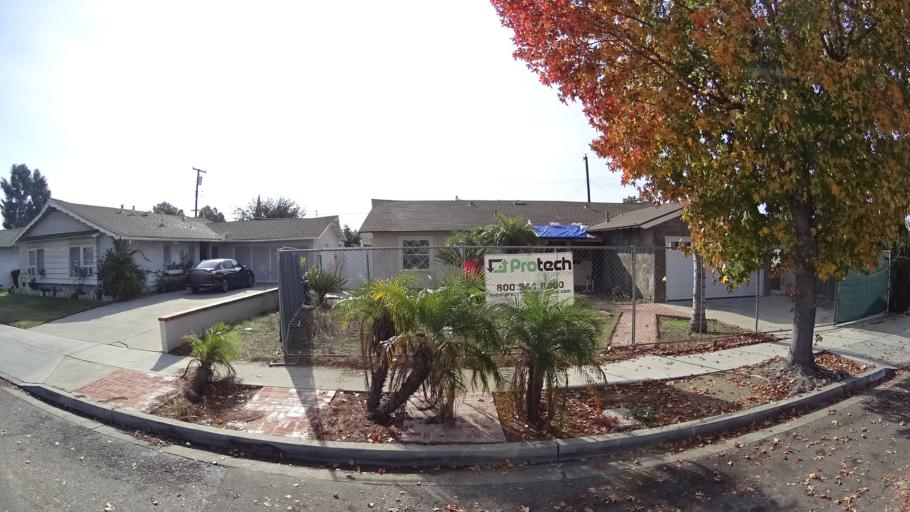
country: US
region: California
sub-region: Orange County
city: Garden Grove
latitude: 33.7918
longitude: -117.9057
